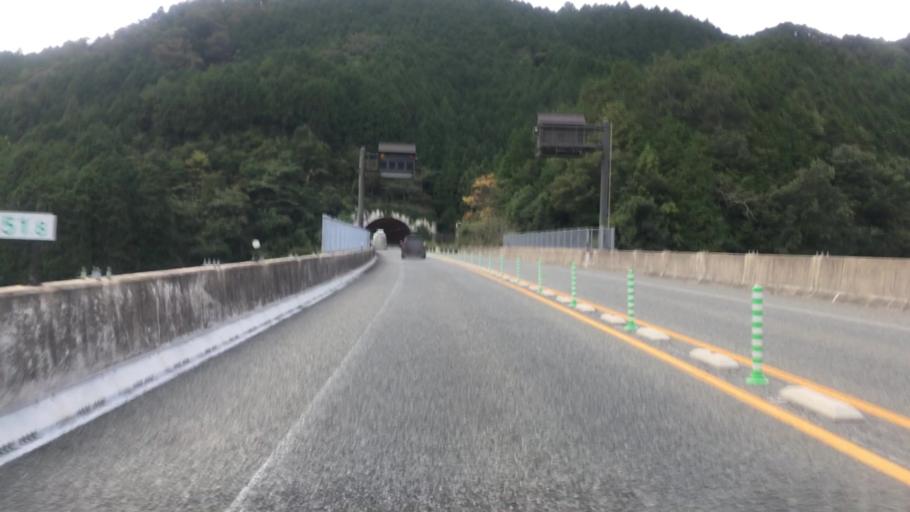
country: JP
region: Kyoto
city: Fukuchiyama
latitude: 35.2640
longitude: 135.0077
